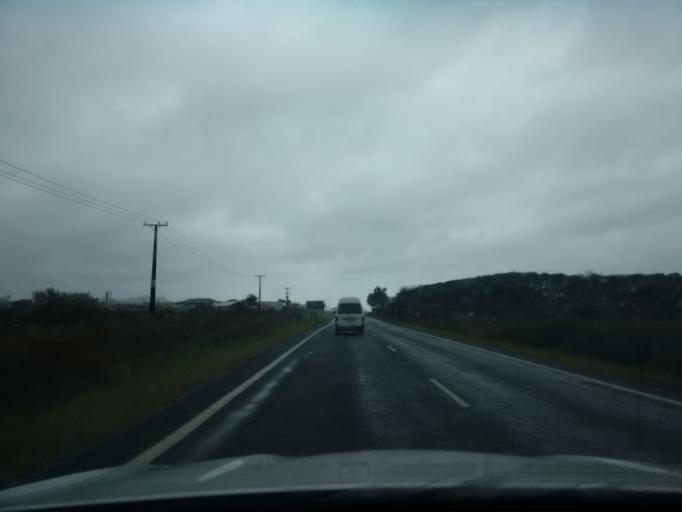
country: NZ
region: Waikato
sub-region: Thames-Coromandel District
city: Whitianga
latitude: -36.8343
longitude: 175.6714
